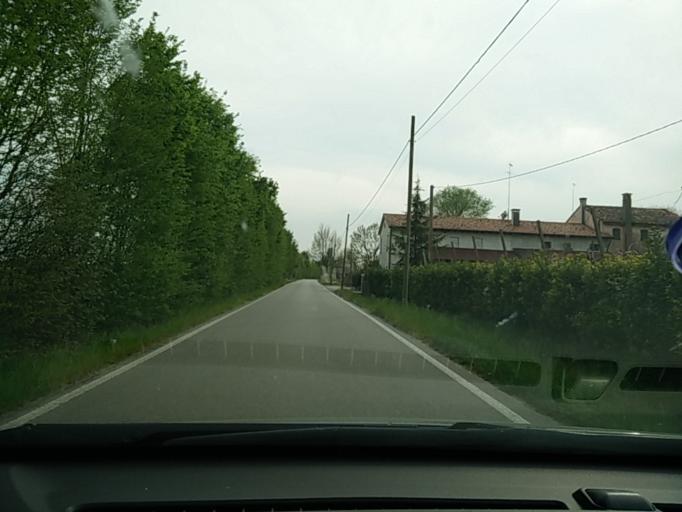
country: IT
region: Veneto
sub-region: Provincia di Treviso
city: Levada
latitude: 45.7440
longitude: 12.4554
